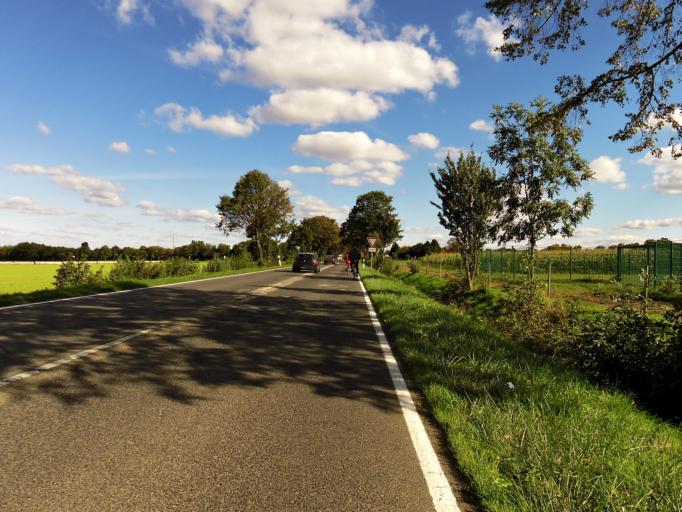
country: DE
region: North Rhine-Westphalia
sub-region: Regierungsbezirk Koln
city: Euskirchen
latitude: 50.6241
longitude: 6.8378
